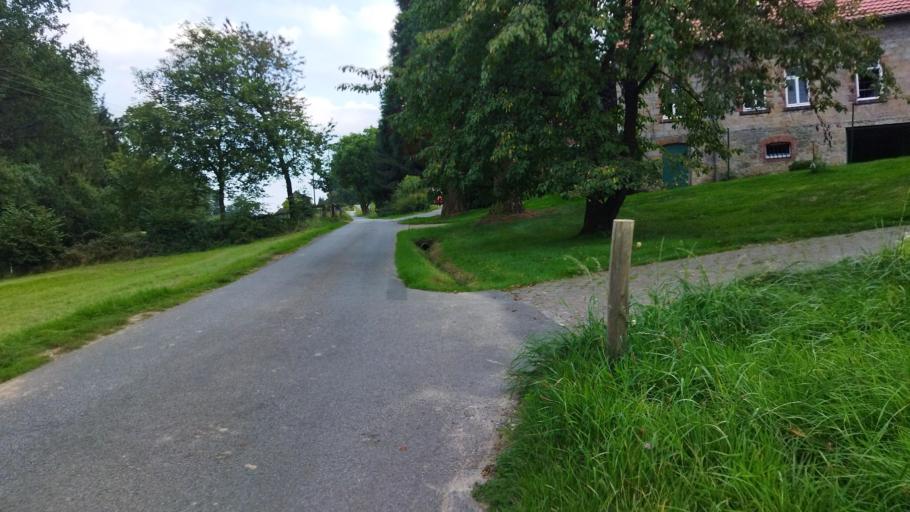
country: DE
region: Lower Saxony
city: Hagen
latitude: 52.1792
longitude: 8.0056
